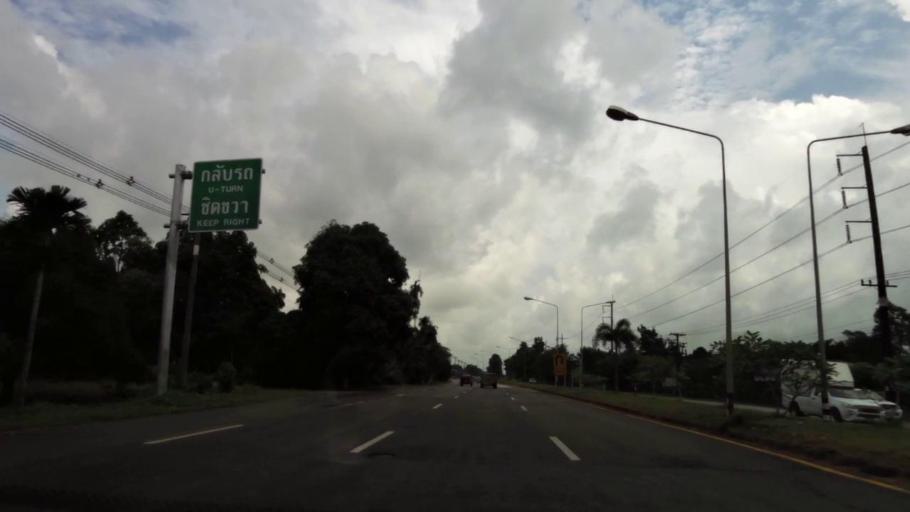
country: TH
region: Chanthaburi
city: Khlung
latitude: 12.5234
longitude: 102.1619
